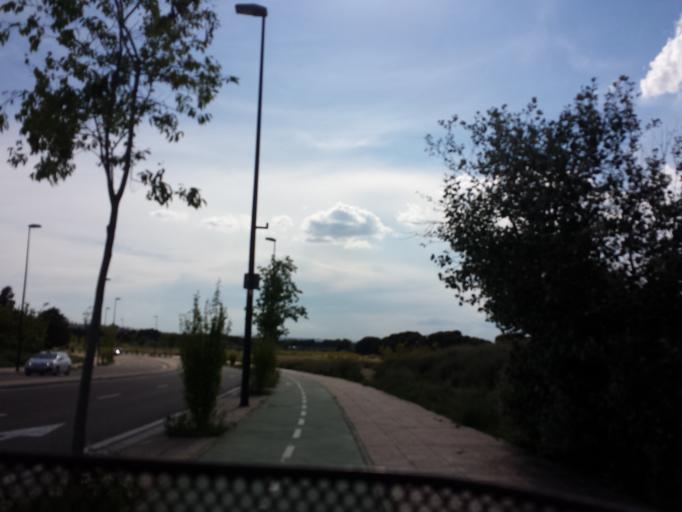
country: ES
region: Aragon
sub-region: Provincia de Zaragoza
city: Oliver-Valdefierro, Oliver, Valdefierro
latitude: 41.6343
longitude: -0.9253
